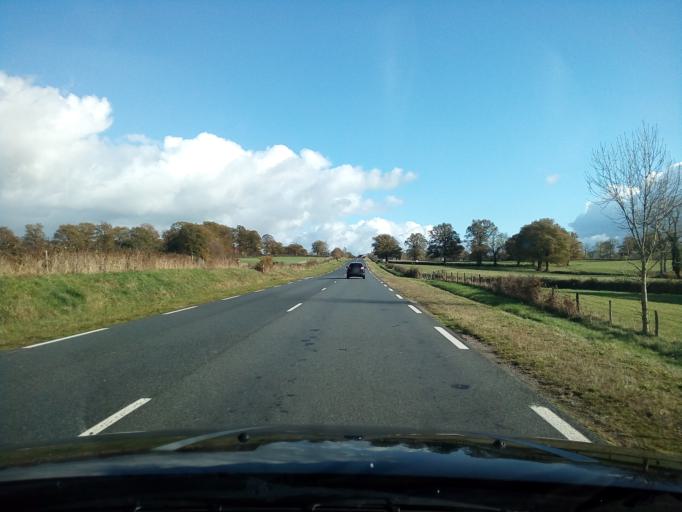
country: FR
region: Auvergne
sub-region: Departement de l'Allier
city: Montmarault
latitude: 46.3220
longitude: 2.9970
